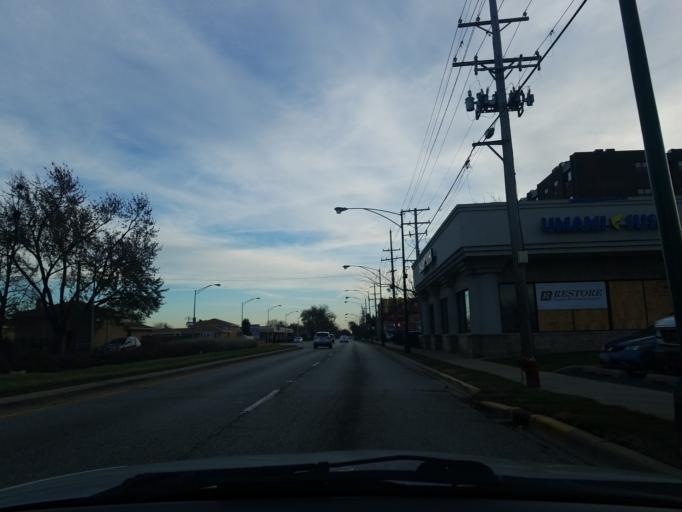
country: US
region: Illinois
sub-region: Cook County
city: Norridge
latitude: 41.9642
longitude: -87.8369
